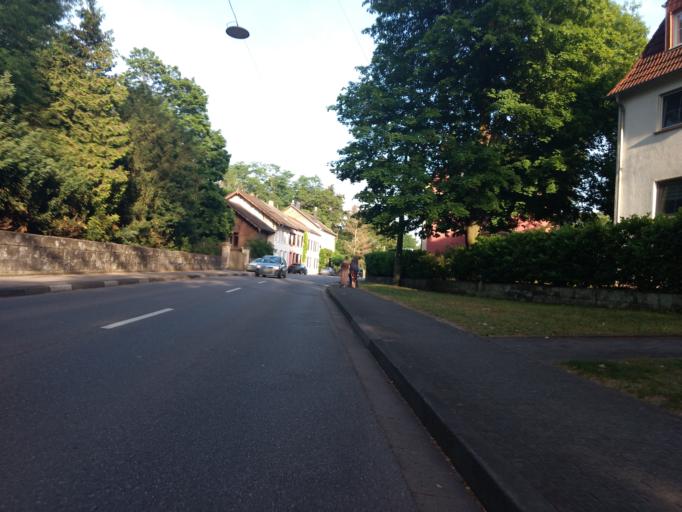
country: DE
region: Saarland
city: Wallerfangen
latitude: 49.3278
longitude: 6.7209
